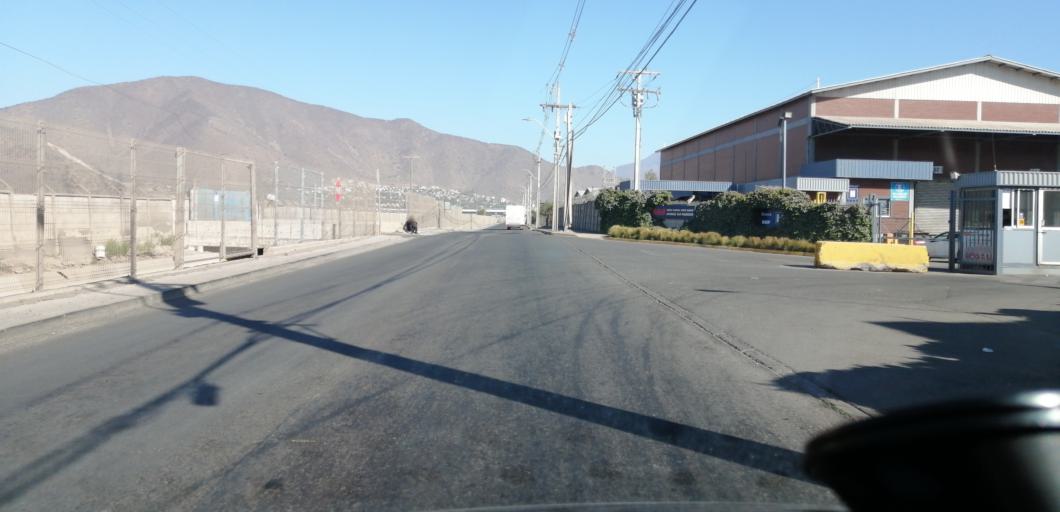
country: CL
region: Santiago Metropolitan
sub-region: Provincia de Santiago
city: Lo Prado
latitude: -33.4568
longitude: -70.7920
